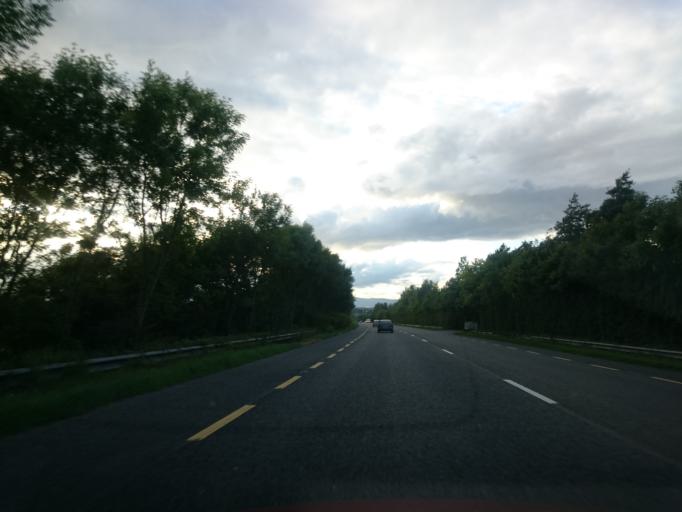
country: IE
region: Leinster
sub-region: Loch Garman
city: Enniscorthy
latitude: 52.4449
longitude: -6.5431
